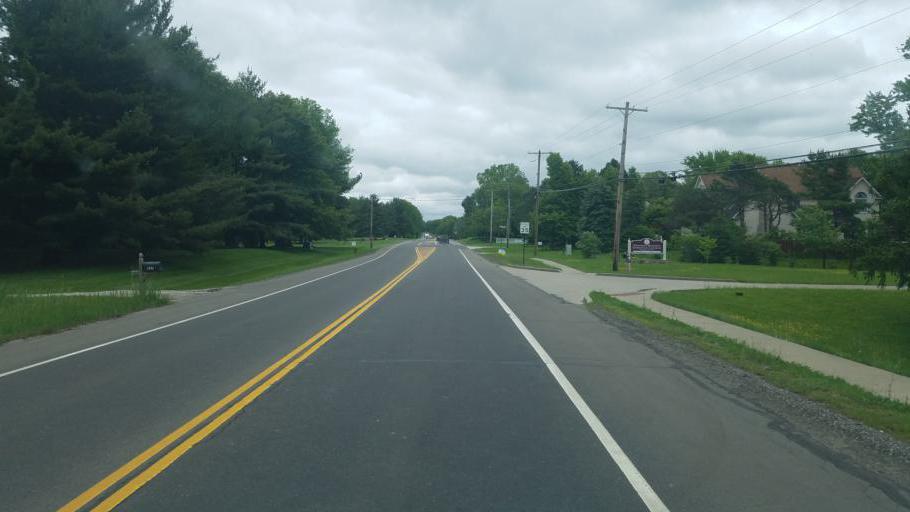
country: US
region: Ohio
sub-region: Summit County
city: Hudson
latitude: 41.2344
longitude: -81.4685
